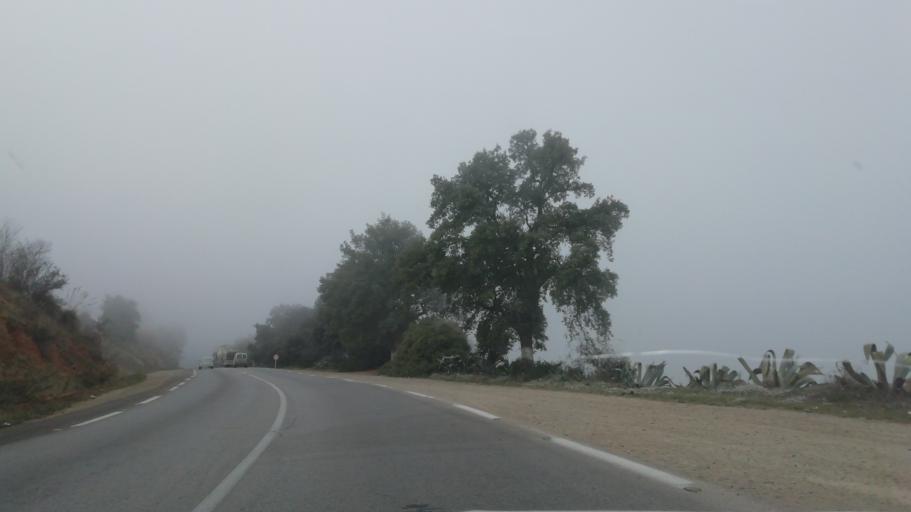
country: DZ
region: Mascara
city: Mascara
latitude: 35.5272
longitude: 0.3369
